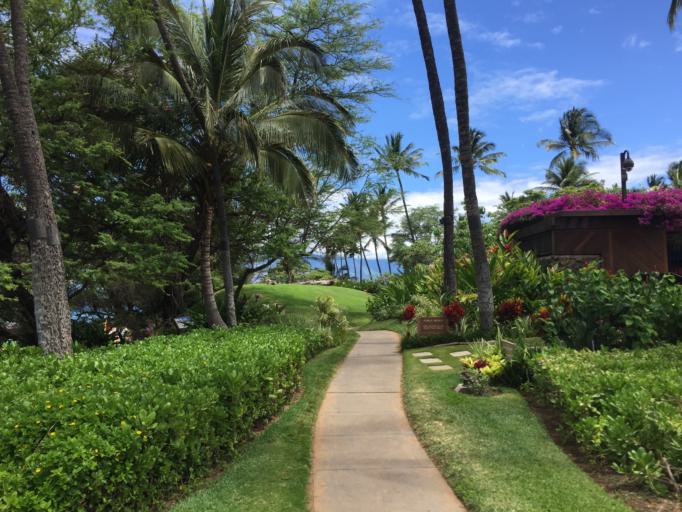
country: US
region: Hawaii
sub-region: Maui County
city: Kihei
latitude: 20.6912
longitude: -156.4438
